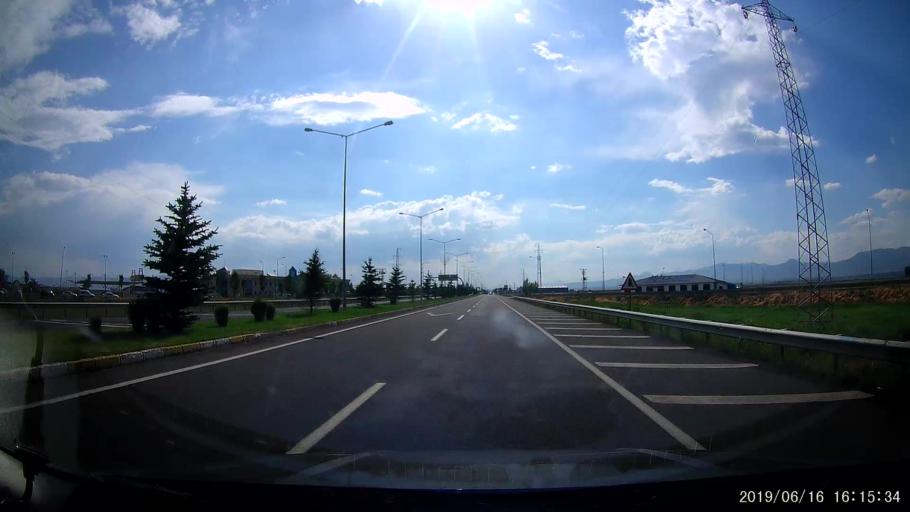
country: TR
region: Erzurum
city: Erzurum
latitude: 39.9620
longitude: 41.2233
